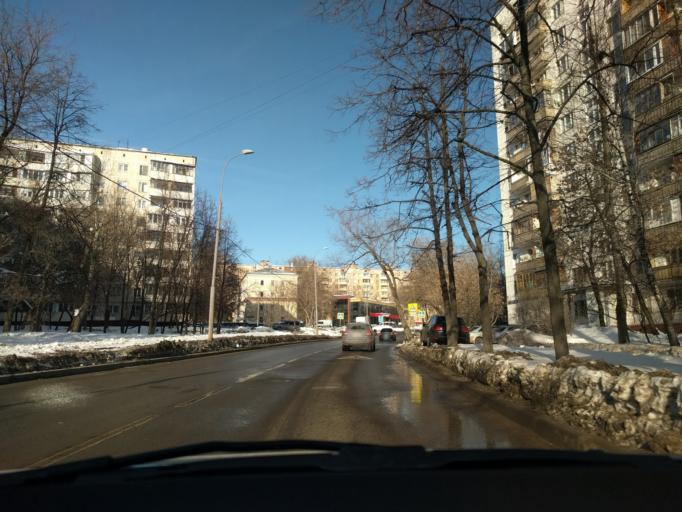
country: RU
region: Moskovskaya
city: Izmaylovo
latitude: 55.7989
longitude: 37.8240
